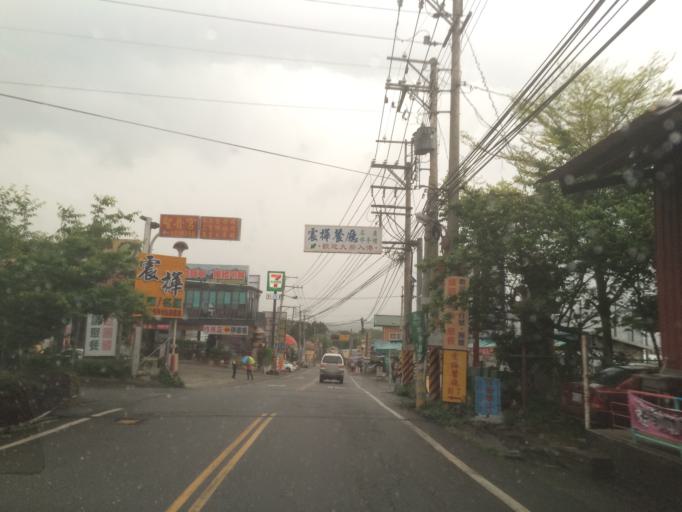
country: TW
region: Taiwan
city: Fengyuan
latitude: 24.1921
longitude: 120.8094
